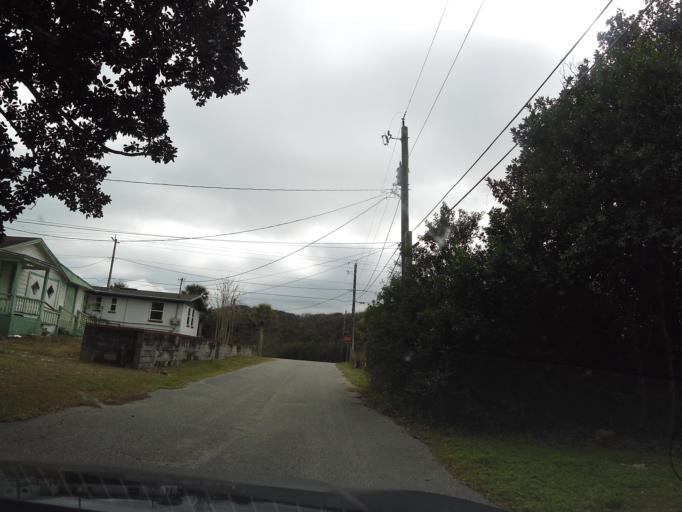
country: US
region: Florida
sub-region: Nassau County
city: Fernandina Beach
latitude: 30.5742
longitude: -81.4462
